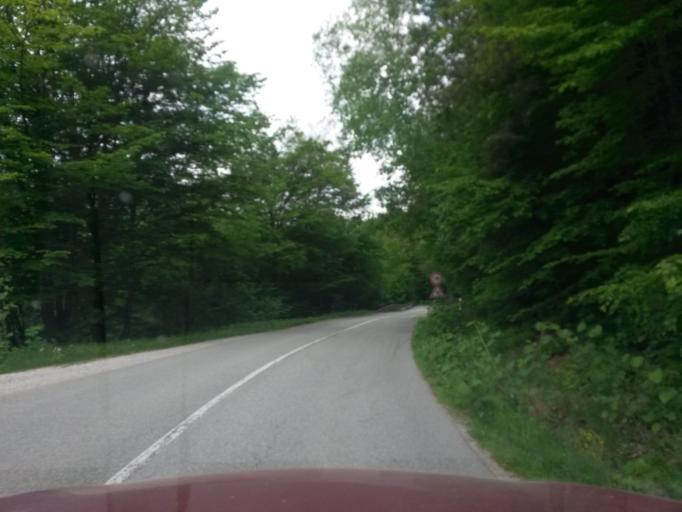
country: SK
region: Kosicky
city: Medzev
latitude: 48.7070
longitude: 20.8105
